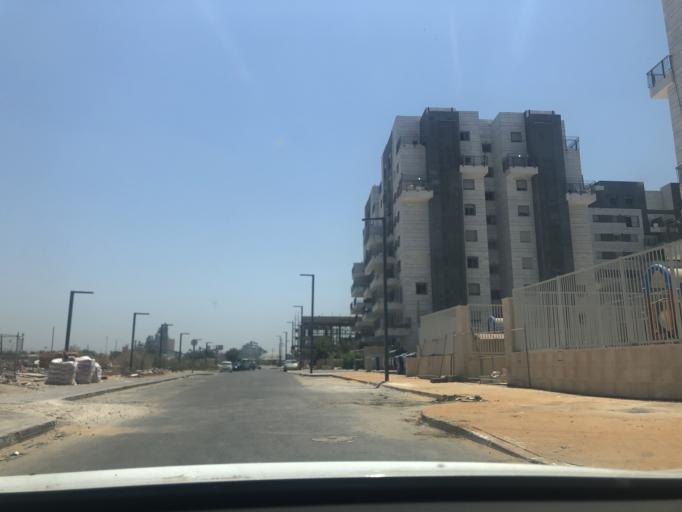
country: IL
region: Central District
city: Lod
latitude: 31.9350
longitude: 34.8990
